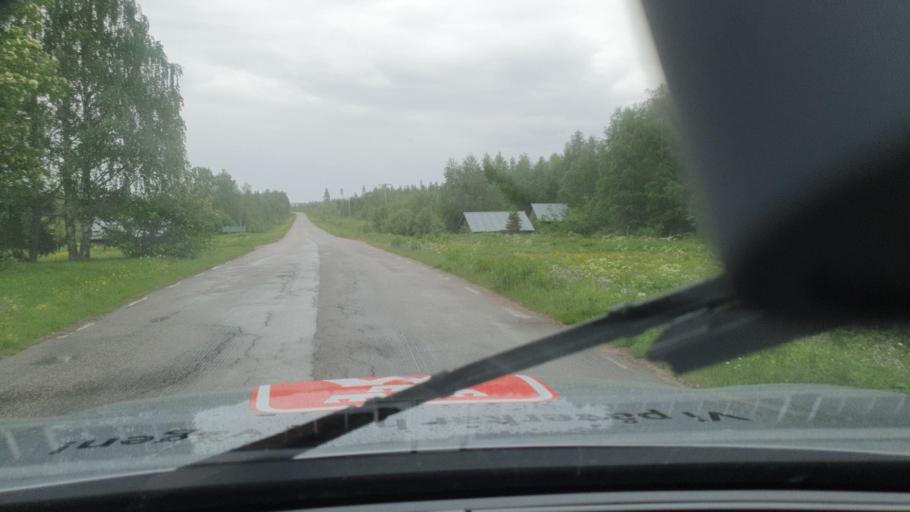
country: SE
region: Norrbotten
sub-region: Pajala Kommun
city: Pajala
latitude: 66.7933
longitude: 23.1252
